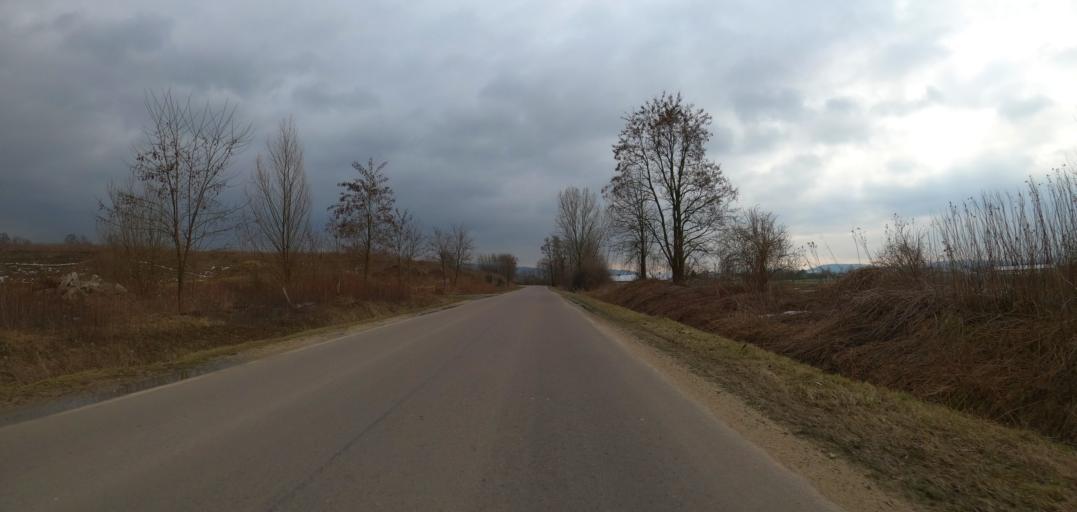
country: PL
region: Subcarpathian Voivodeship
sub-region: Powiat debicki
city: Pilzno
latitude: 49.9832
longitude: 21.3281
